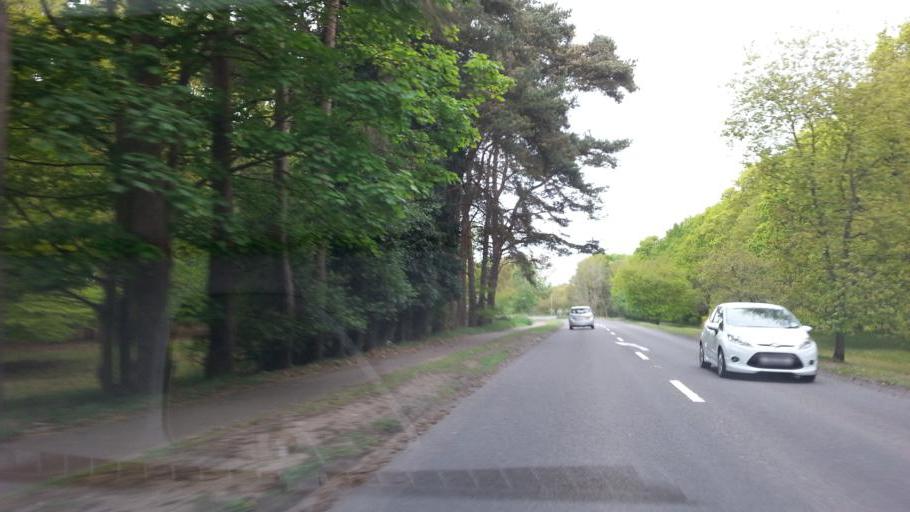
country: GB
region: England
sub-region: Suffolk
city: Lakenheath
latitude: 52.3398
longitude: 0.5307
